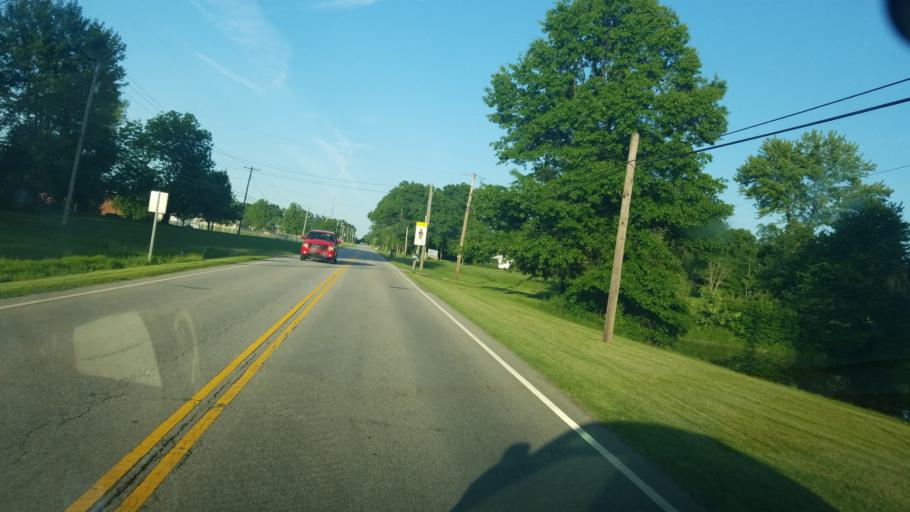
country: US
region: Ohio
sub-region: Mahoning County
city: Craig Beach
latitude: 41.0993
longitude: -80.9202
